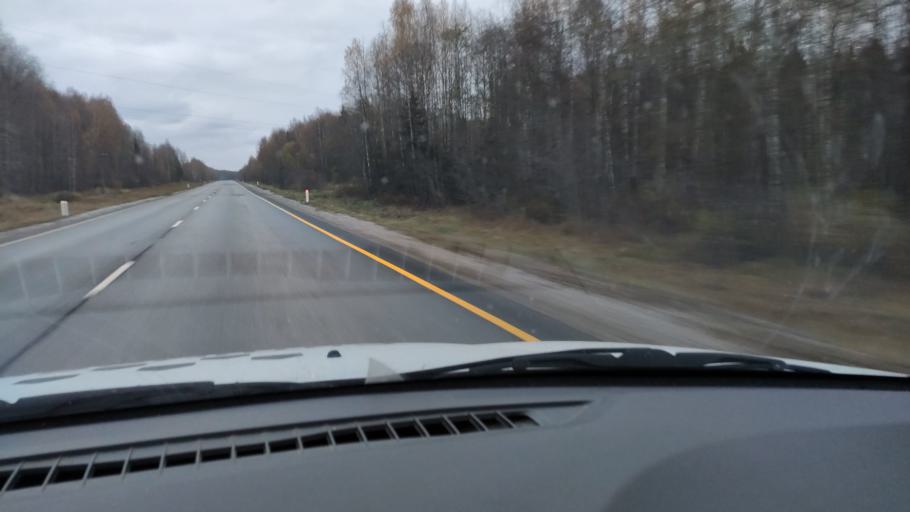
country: RU
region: Kirov
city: Kostino
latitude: 58.8137
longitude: 52.9420
